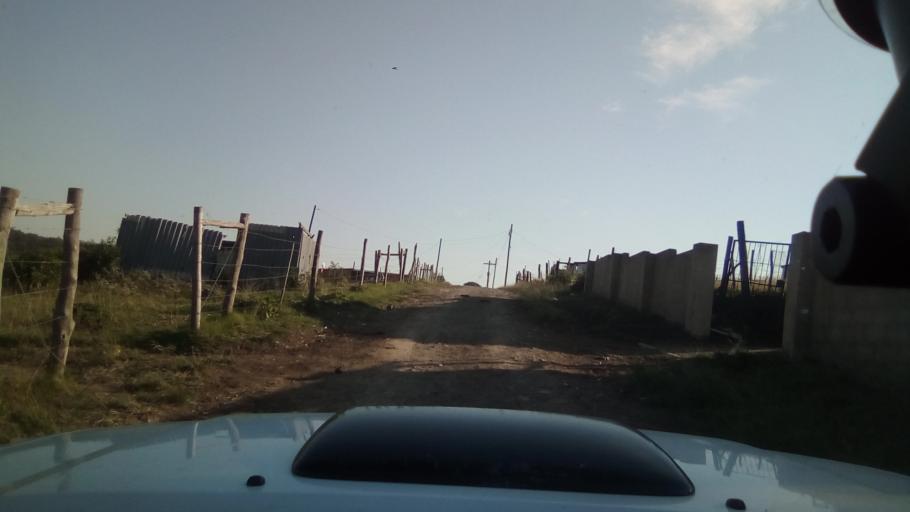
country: ZA
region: Eastern Cape
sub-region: Buffalo City Metropolitan Municipality
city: East London
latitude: -32.8466
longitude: 27.9859
